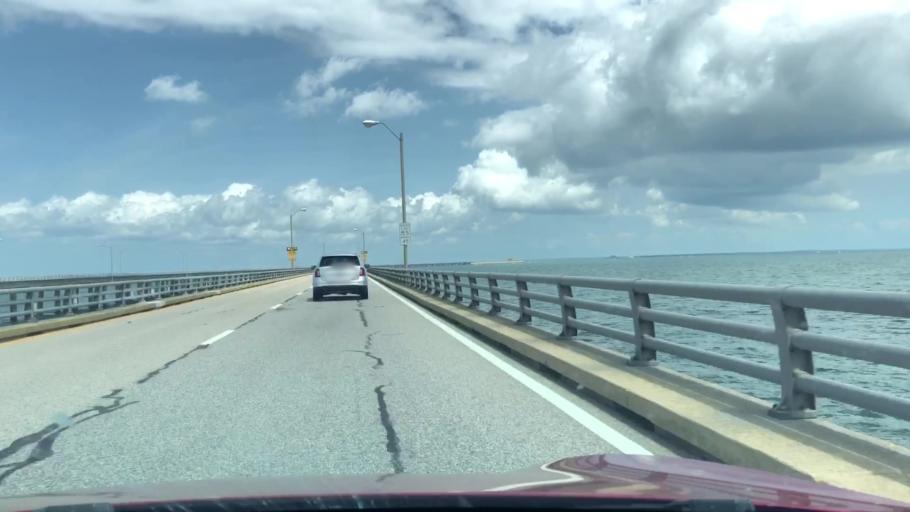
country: US
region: Virginia
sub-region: City of Virginia Beach
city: Virginia Beach
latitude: 37.0112
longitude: -76.0936
